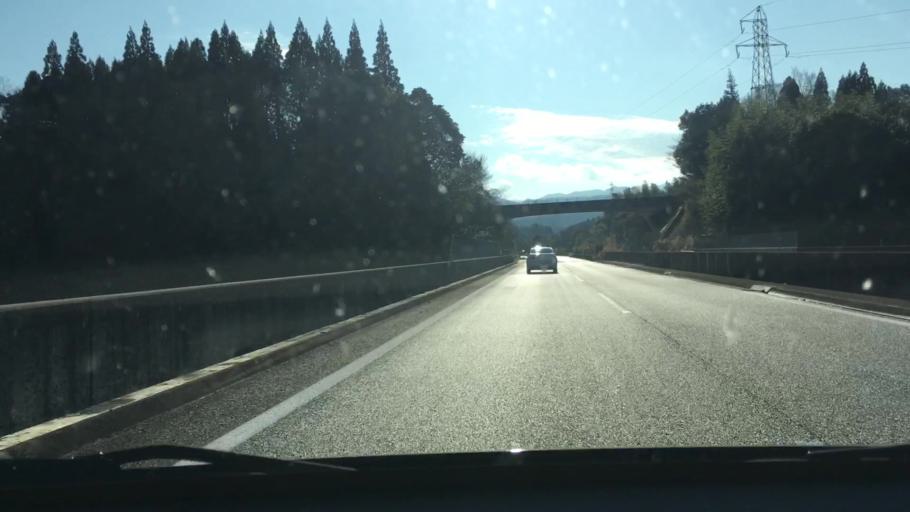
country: JP
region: Kumamoto
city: Hitoyoshi
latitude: 32.2128
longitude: 130.7762
